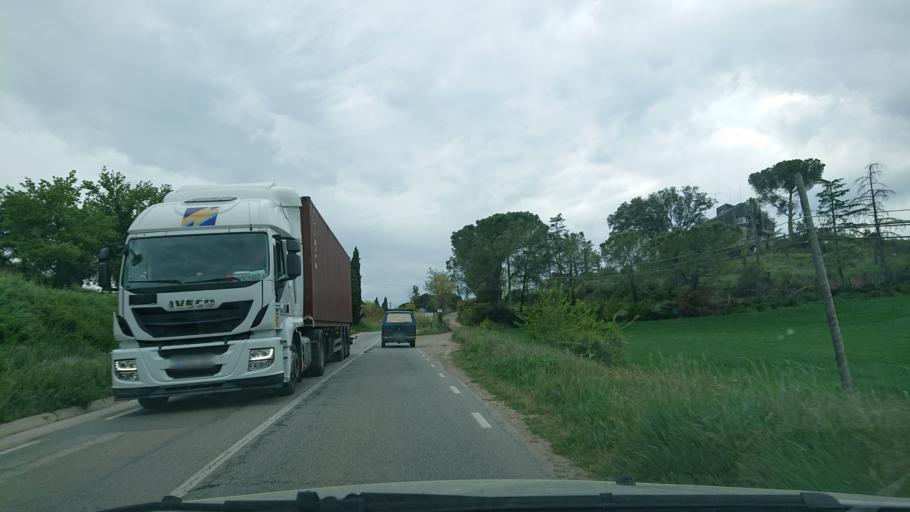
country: ES
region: Catalonia
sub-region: Provincia de Barcelona
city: Sant Pere de Vilamajor
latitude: 41.6755
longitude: 2.3905
